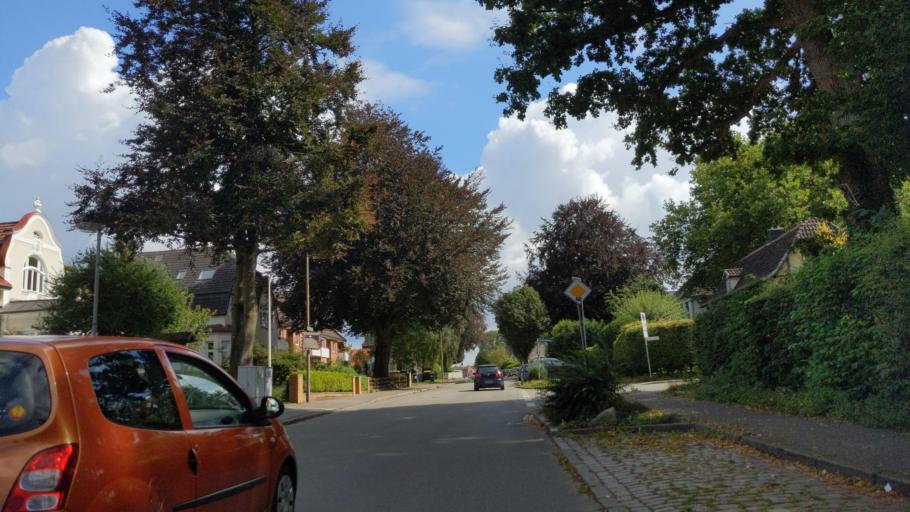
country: DE
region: Schleswig-Holstein
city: Reinfeld
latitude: 53.8279
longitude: 10.4943
